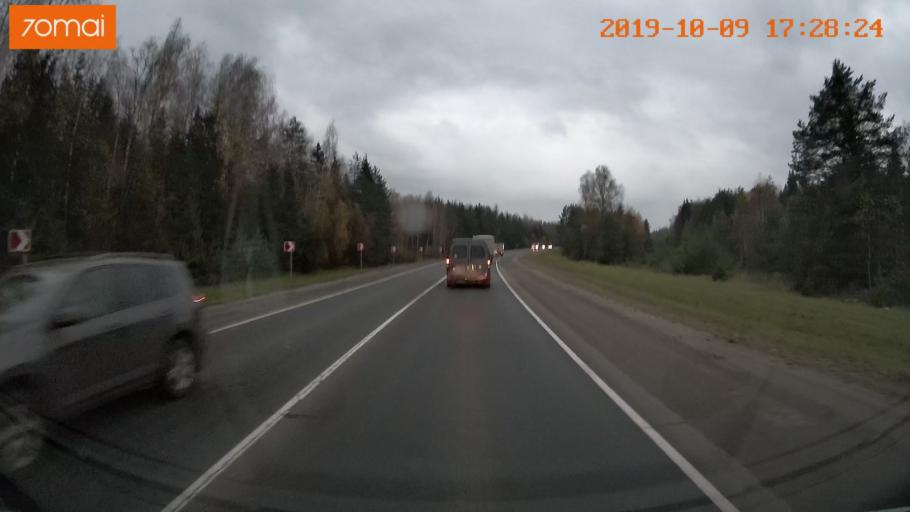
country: RU
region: Ivanovo
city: Furmanov
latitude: 57.1582
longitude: 41.0685
